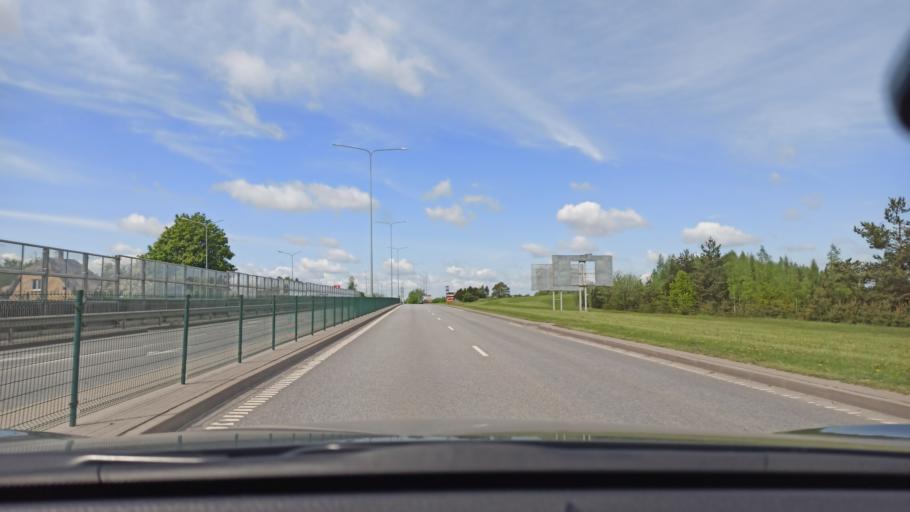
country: LT
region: Siauliu apskritis
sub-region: Siauliai
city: Siauliai
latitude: 55.9229
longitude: 23.3628
